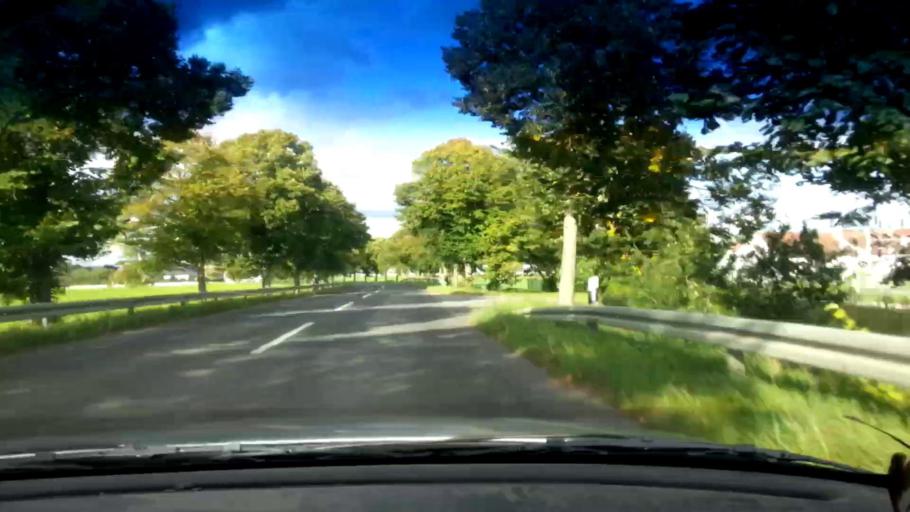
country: DE
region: Bavaria
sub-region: Upper Franconia
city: Ebensfeld
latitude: 50.0620
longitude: 10.9500
